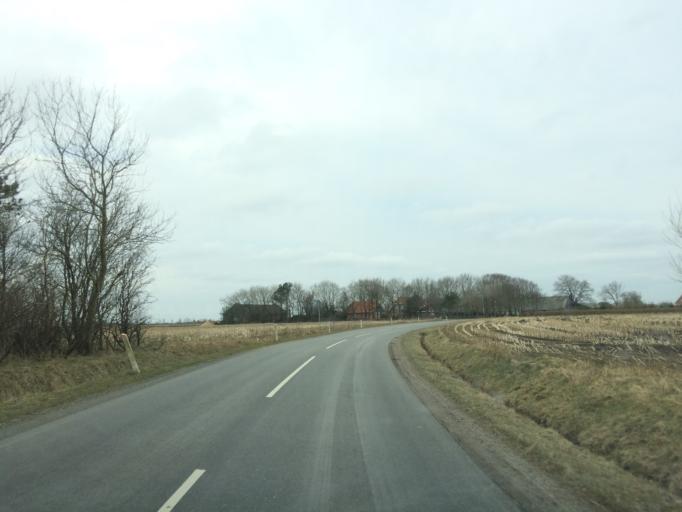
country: DK
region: South Denmark
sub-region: Varde Kommune
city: Oksbol
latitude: 55.7913
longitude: 8.3425
